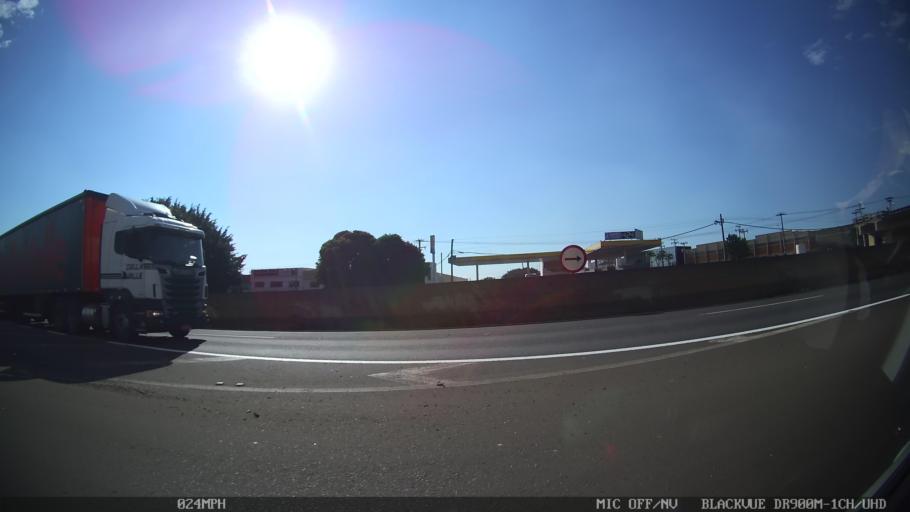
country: BR
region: Sao Paulo
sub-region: Santa Barbara D'Oeste
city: Santa Barbara d'Oeste
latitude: -22.7647
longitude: -47.3897
